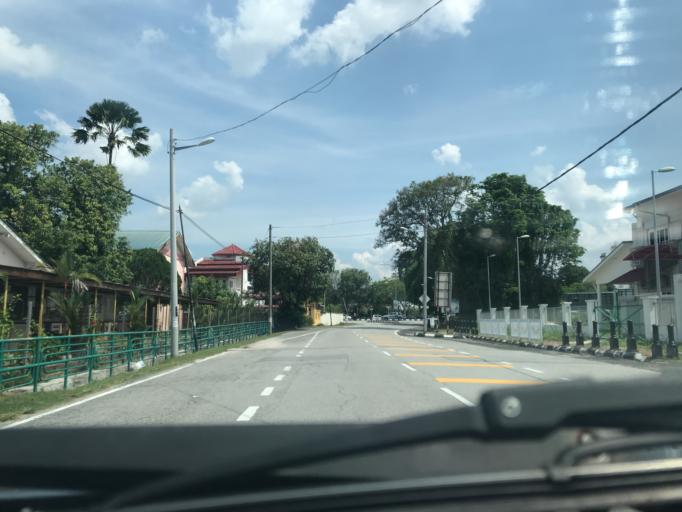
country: MY
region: Perak
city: Ipoh
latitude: 4.6029
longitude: 101.0983
